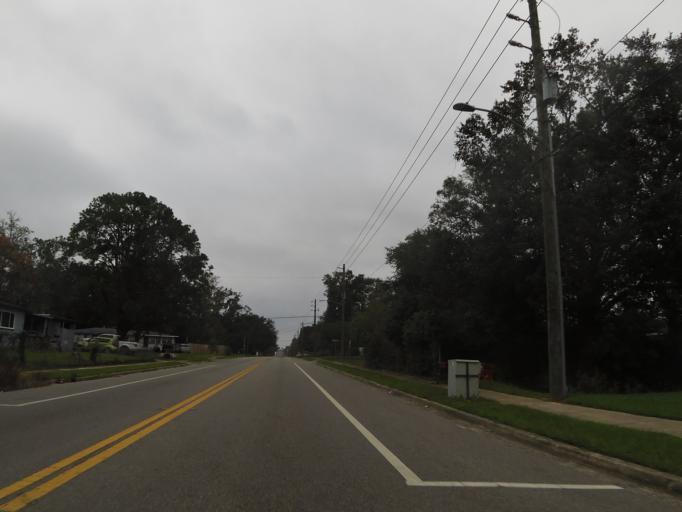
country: US
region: Florida
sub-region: Clay County
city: Bellair-Meadowbrook Terrace
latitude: 30.2536
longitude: -81.7473
